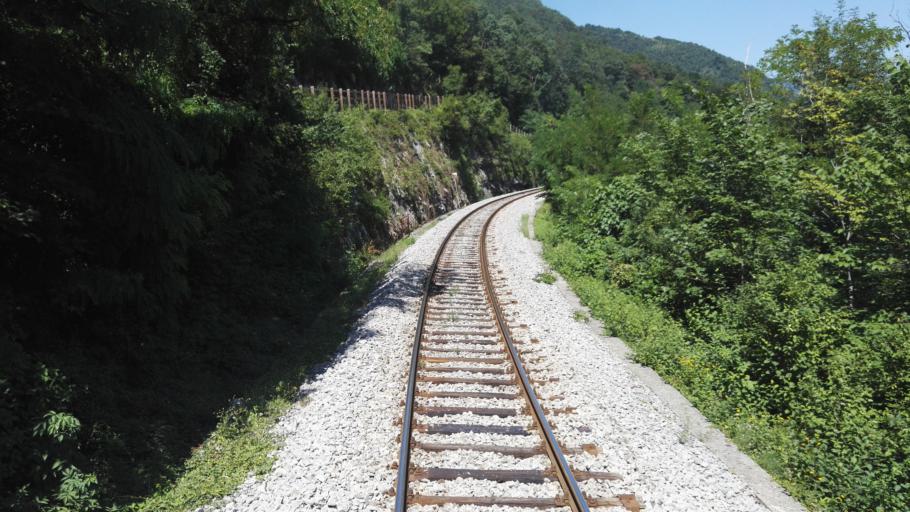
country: IT
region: Friuli Venezia Giulia
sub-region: Provincia di Gorizia
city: San Floriano del Collio
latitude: 46.0101
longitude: 13.6136
